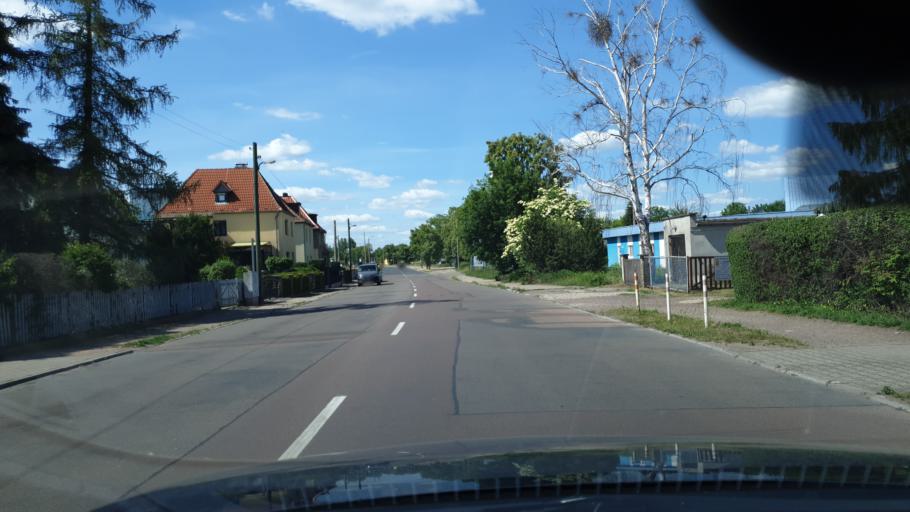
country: DE
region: Saxony-Anhalt
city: Dessau
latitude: 51.8096
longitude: 12.2552
